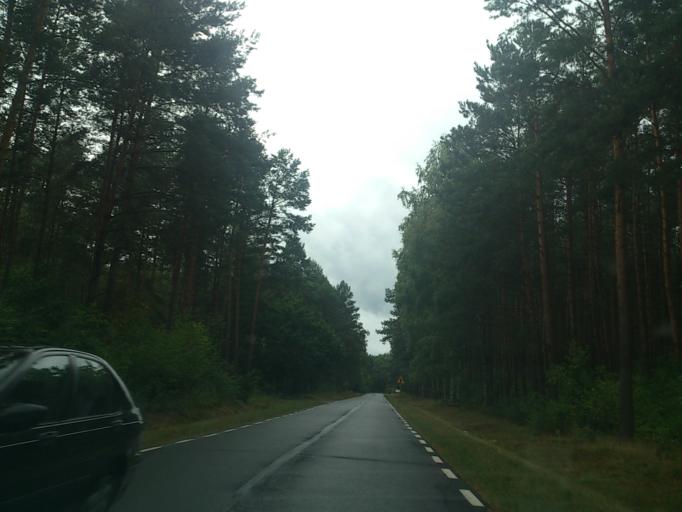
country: PL
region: Greater Poland Voivodeship
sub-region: Powiat gnieznienski
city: Kiszkowo
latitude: 52.5188
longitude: 17.1817
